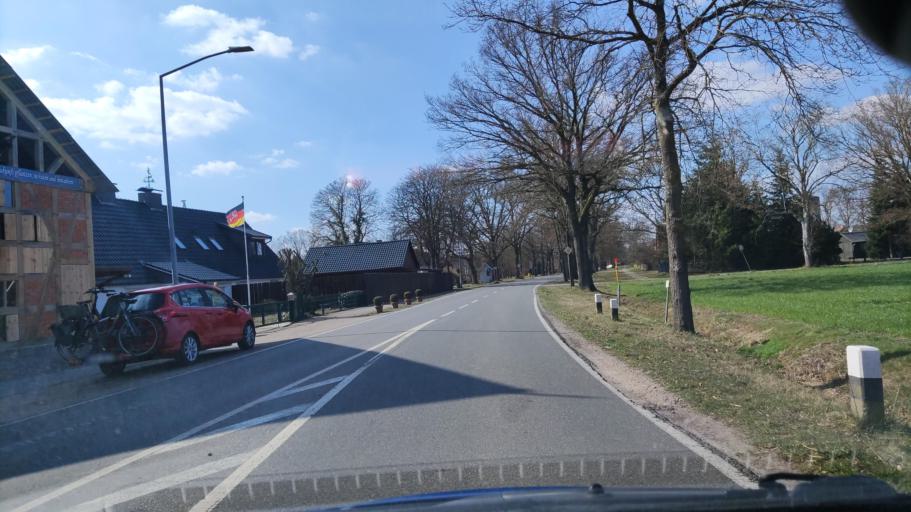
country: DE
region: Lower Saxony
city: Trebel
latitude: 53.0303
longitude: 11.3077
